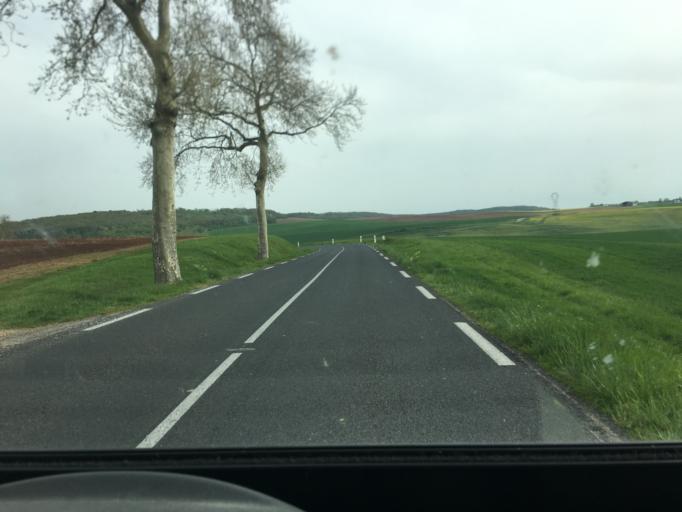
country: FR
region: Lorraine
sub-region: Departement de Meurthe-et-Moselle
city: Einville-au-Jard
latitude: 48.6857
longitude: 6.5023
